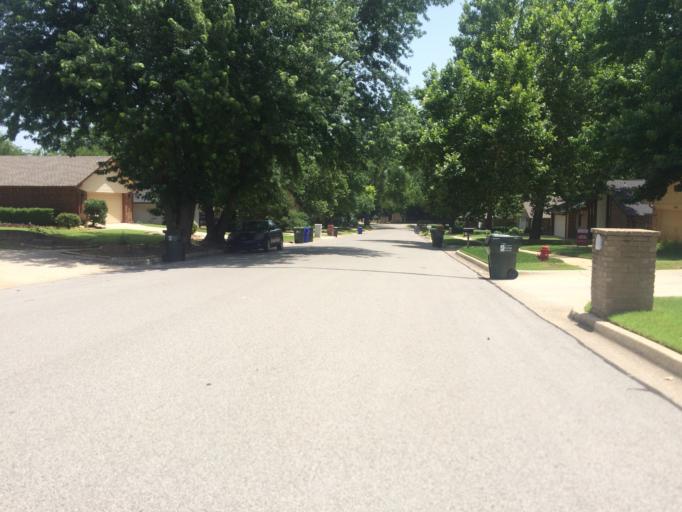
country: US
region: Oklahoma
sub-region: Cleveland County
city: Norman
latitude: 35.1887
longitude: -97.4665
